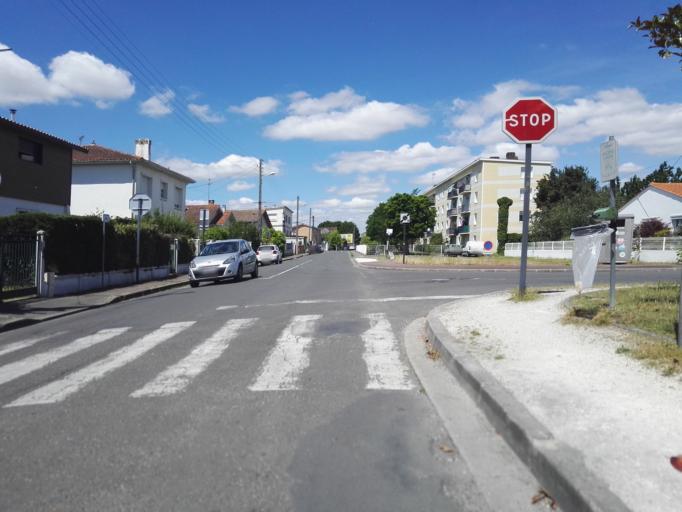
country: FR
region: Aquitaine
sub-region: Departement de la Gironde
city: Talence
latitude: 44.8036
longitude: -0.5784
